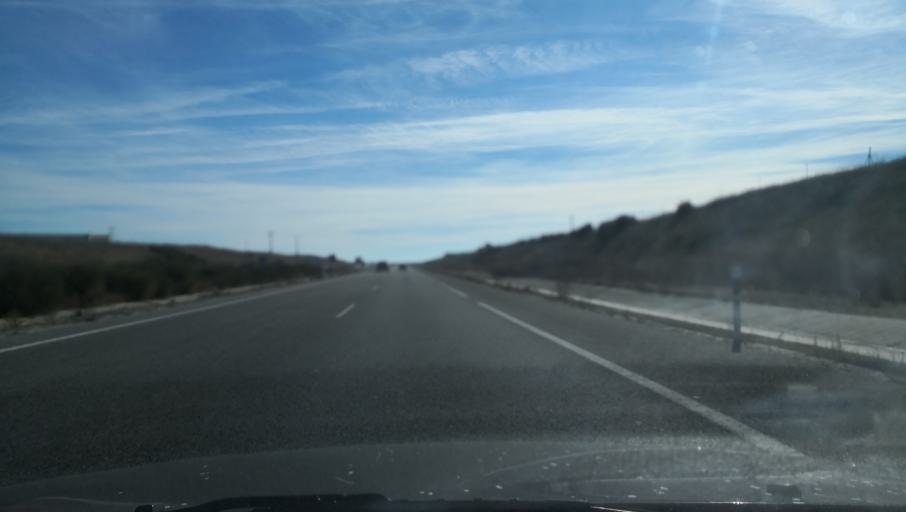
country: ES
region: Castille and Leon
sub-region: Provincia de Salamanca
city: Penaranda de Bracamonte
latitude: 40.9079
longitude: -5.1824
